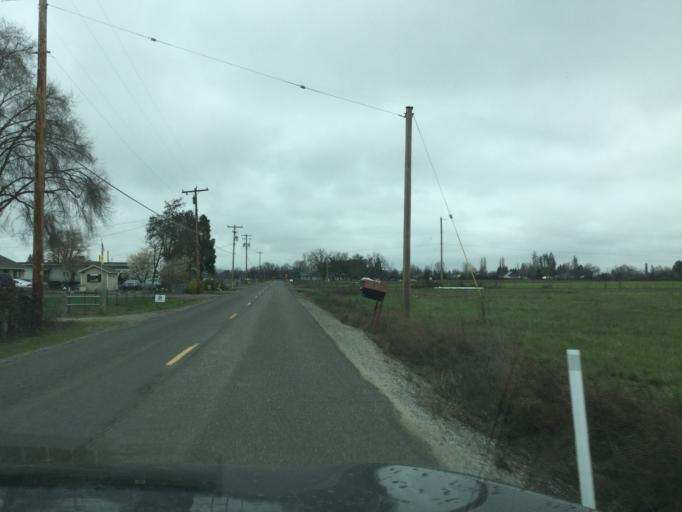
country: US
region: Oregon
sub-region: Jackson County
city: Central Point
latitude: 42.3898
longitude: -122.9461
